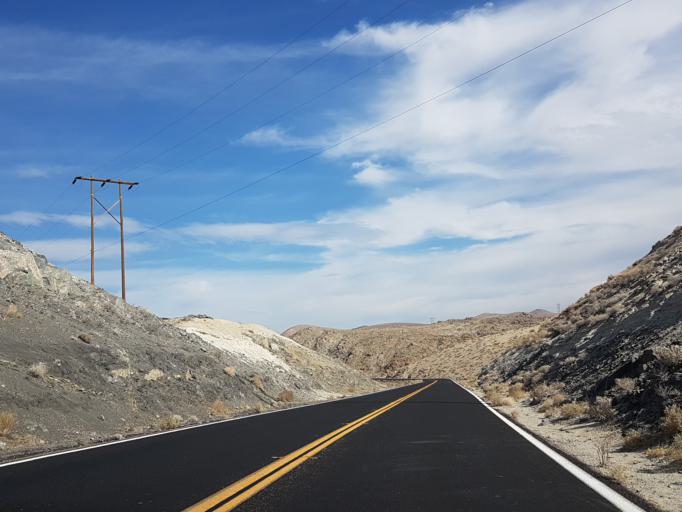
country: US
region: California
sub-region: San Bernardino County
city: Searles Valley
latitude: 35.6548
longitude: -117.4607
